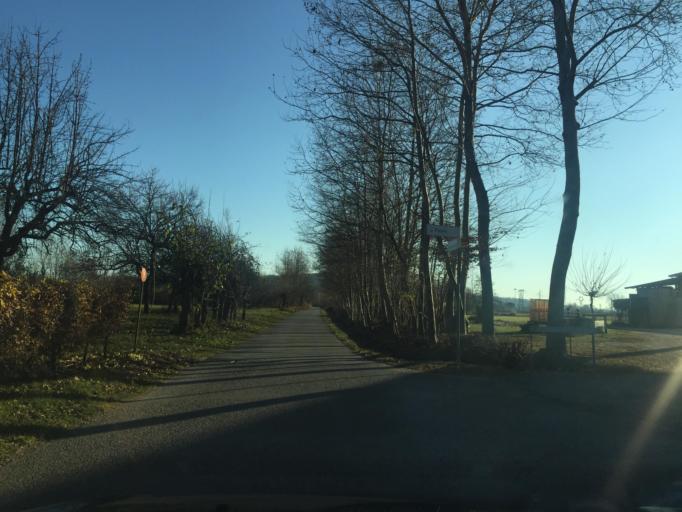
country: IT
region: Friuli Venezia Giulia
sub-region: Provincia di Udine
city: Osoppo
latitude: 46.2452
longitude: 13.1103
